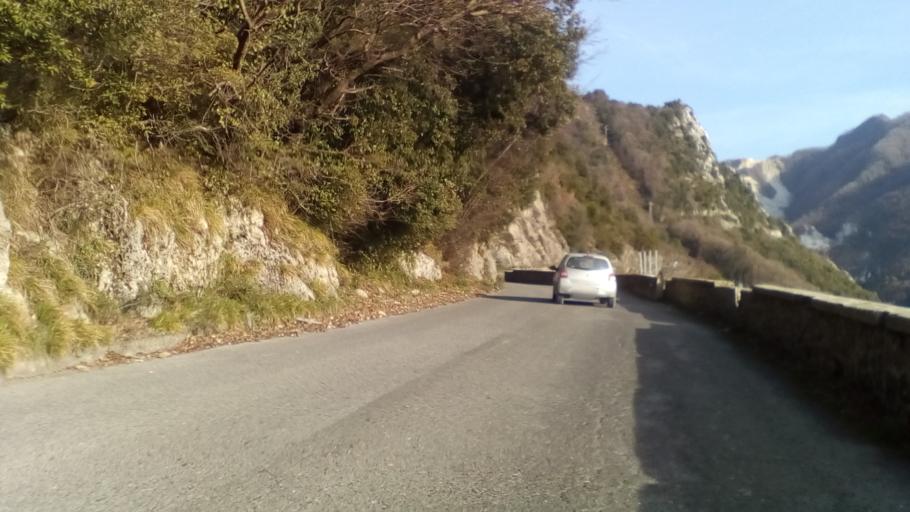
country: IT
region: Tuscany
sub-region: Provincia di Massa-Carrara
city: Massa
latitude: 44.0835
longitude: 10.1192
